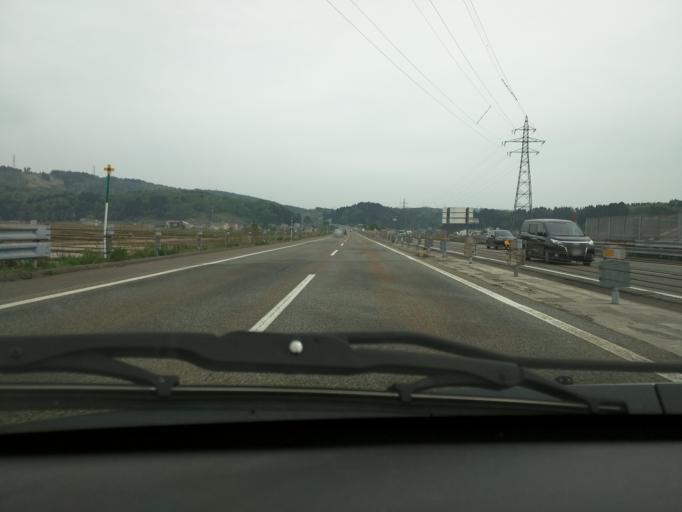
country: JP
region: Niigata
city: Ojiya
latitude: 37.2960
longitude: 138.7821
